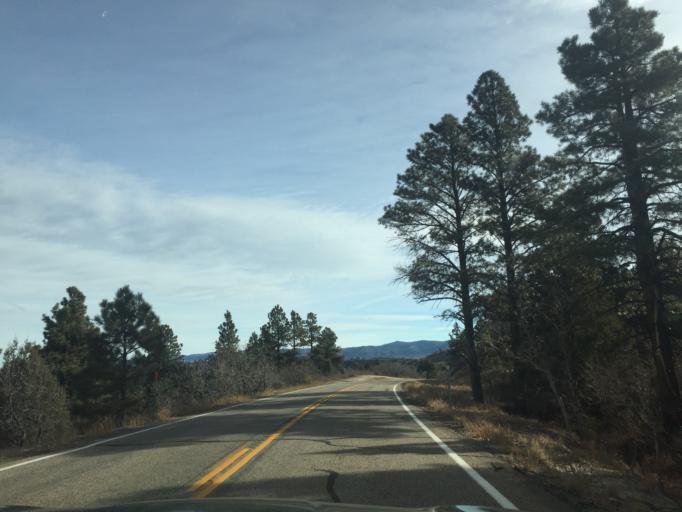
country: US
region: Utah
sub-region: Garfield County
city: Panguitch
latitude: 37.4967
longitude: -112.5478
